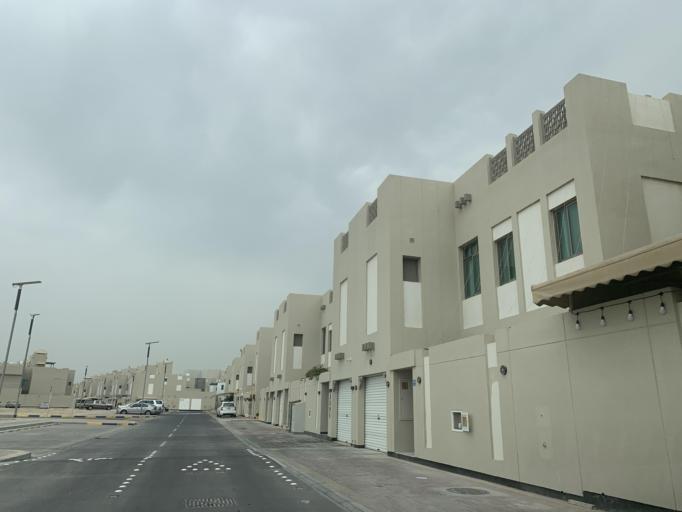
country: BH
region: Northern
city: Madinat `Isa
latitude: 26.1693
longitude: 50.5091
